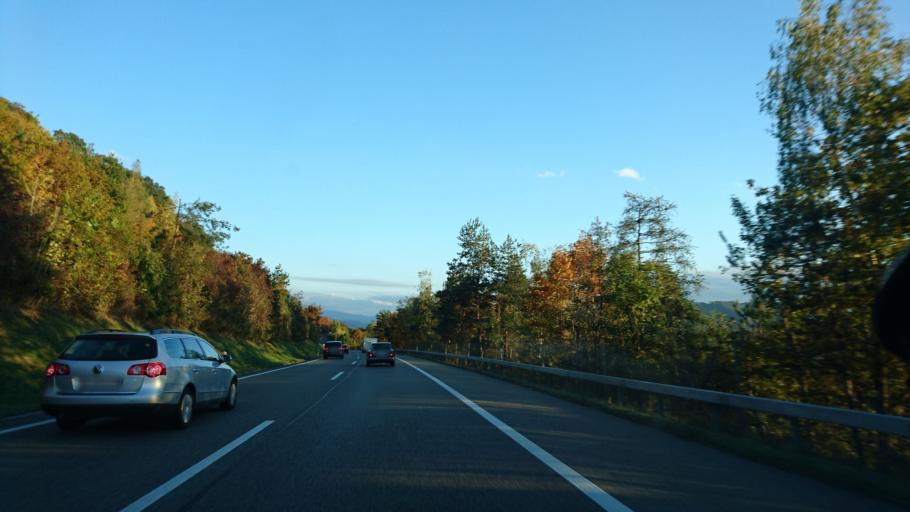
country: CH
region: Bern
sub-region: Bern-Mittelland District
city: Belp
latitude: 46.9133
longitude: 7.5138
